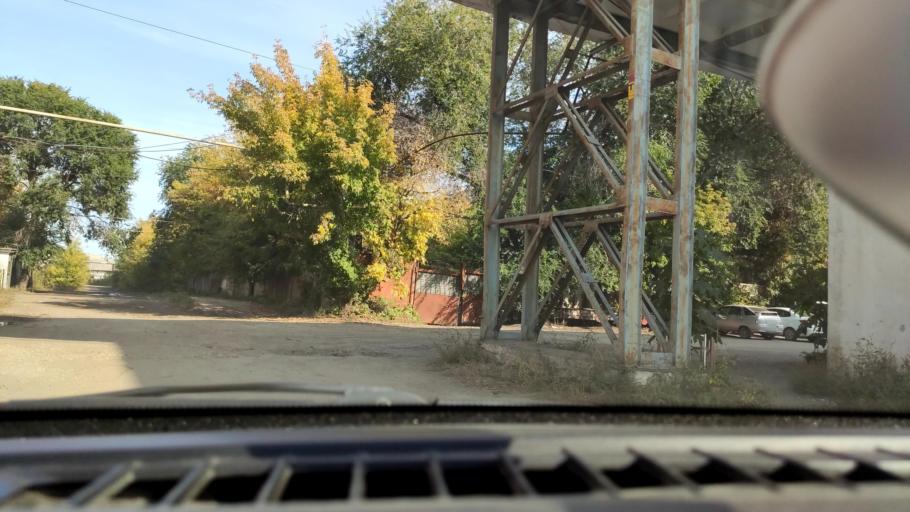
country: RU
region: Samara
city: Samara
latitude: 53.1895
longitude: 50.2602
